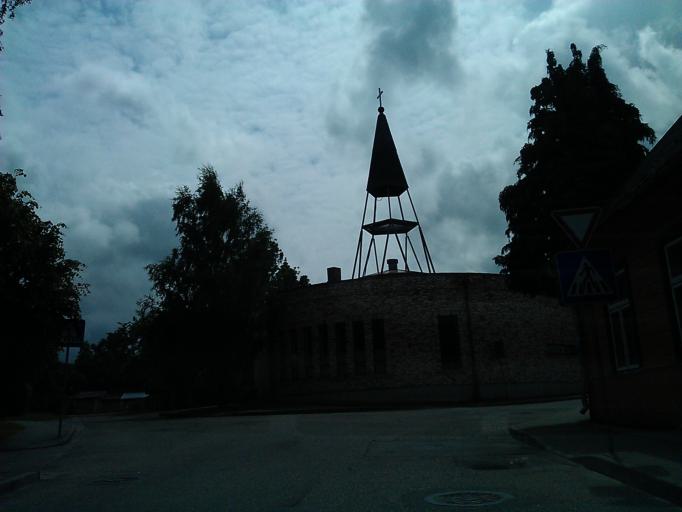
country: LV
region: Aizpute
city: Aizpute
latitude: 56.7221
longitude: 21.6050
